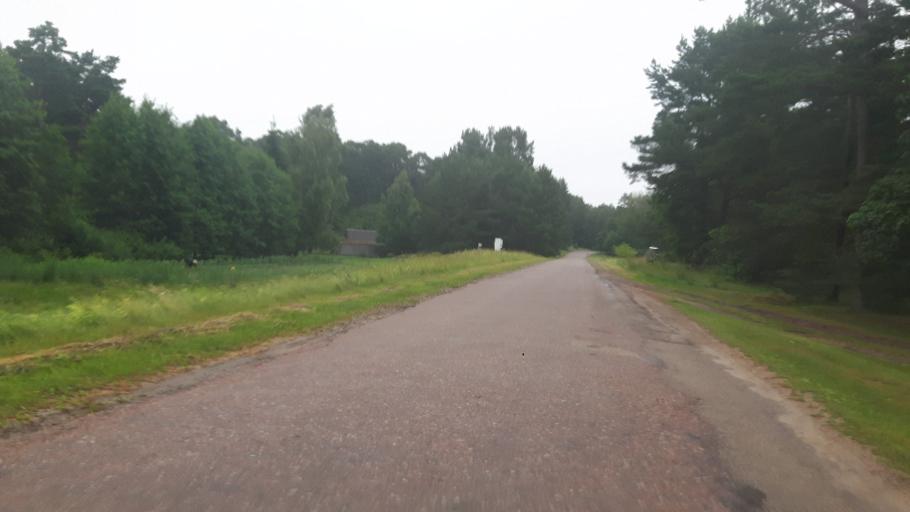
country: LV
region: Nica
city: Nica
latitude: 56.3812
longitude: 20.9886
